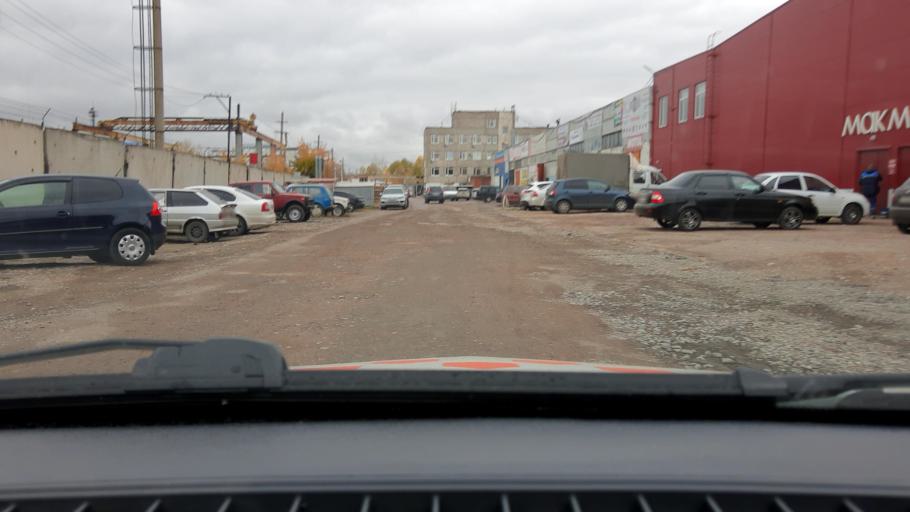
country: RU
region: Bashkortostan
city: Ufa
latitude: 54.7893
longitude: 56.0898
